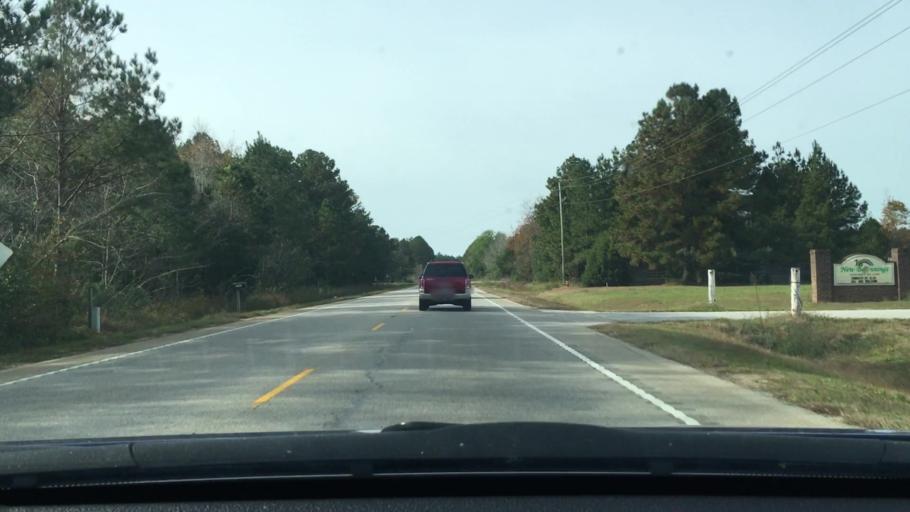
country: US
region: South Carolina
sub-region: Sumter County
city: Cherryvale
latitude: 33.9407
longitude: -80.4824
